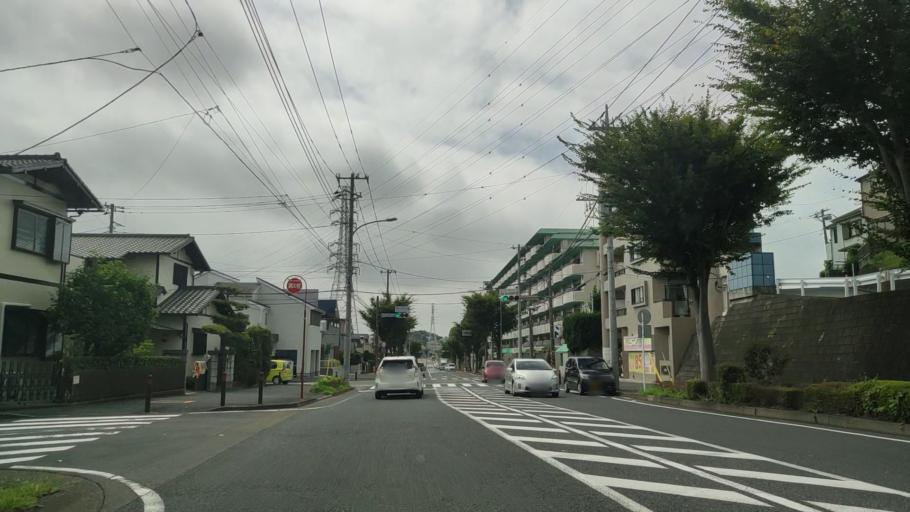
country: JP
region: Kanagawa
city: Fujisawa
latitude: 35.4161
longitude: 139.5227
